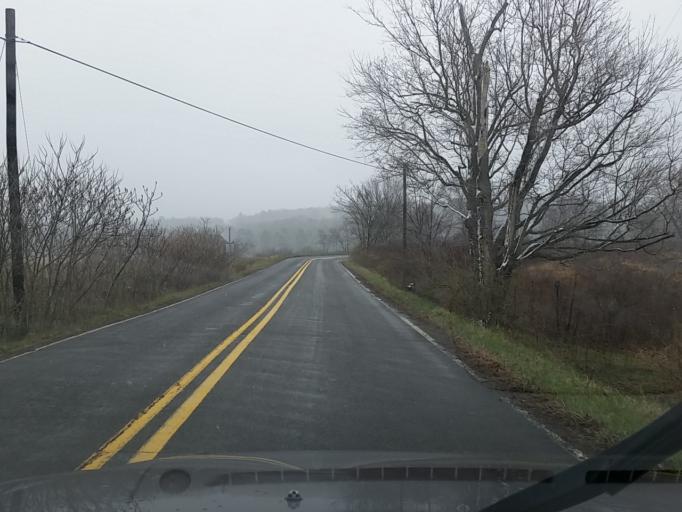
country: US
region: Pennsylvania
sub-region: Luzerne County
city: East Berwick
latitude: 41.1918
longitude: -76.2135
